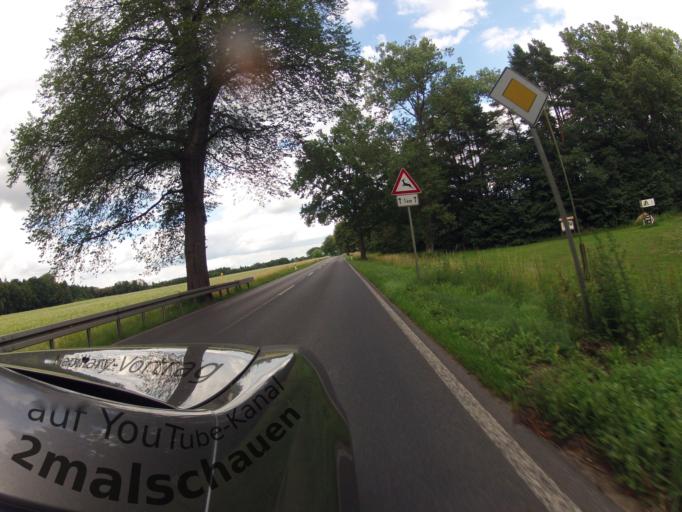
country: DE
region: Mecklenburg-Vorpommern
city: Anklam
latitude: 53.8983
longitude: 13.7338
